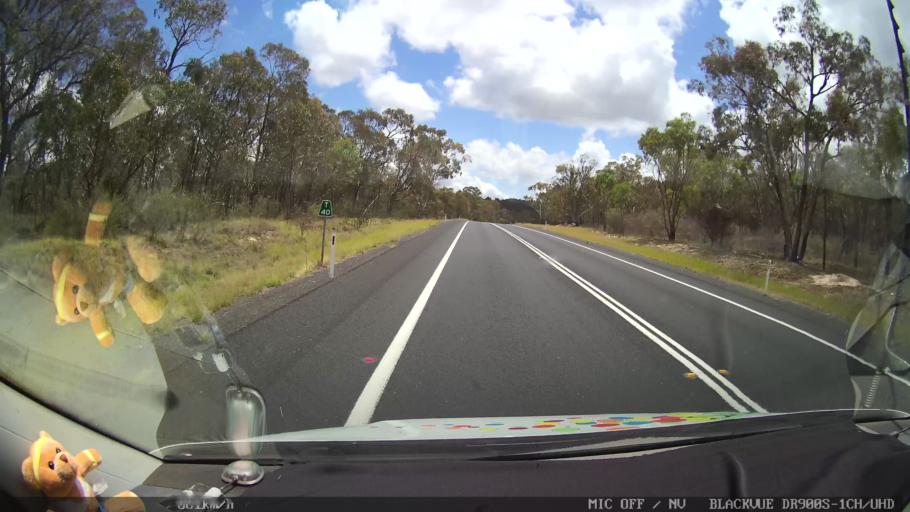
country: AU
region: New South Wales
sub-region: Glen Innes Severn
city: Glen Innes
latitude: -29.3584
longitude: 151.8980
